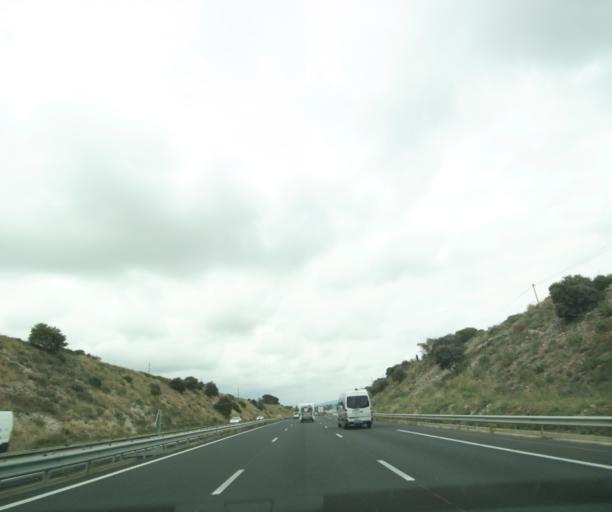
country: FR
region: Languedoc-Roussillon
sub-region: Departement de l'Herault
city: Poussan
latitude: 43.4763
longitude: 3.6529
